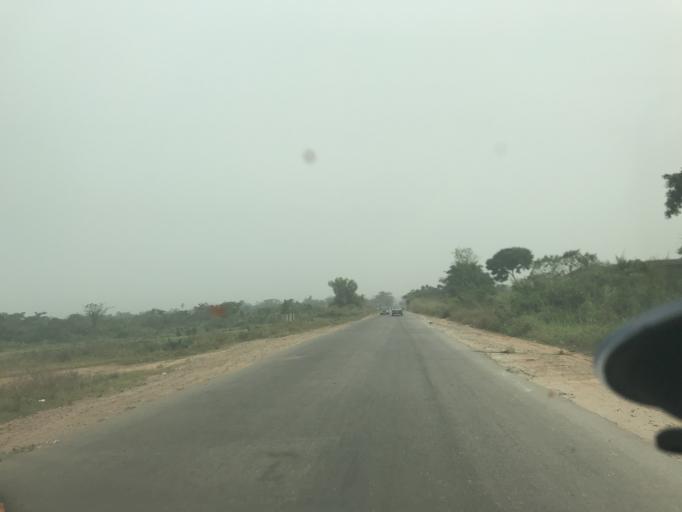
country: NG
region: Ogun
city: Itori
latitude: 6.8886
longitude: 3.1488
